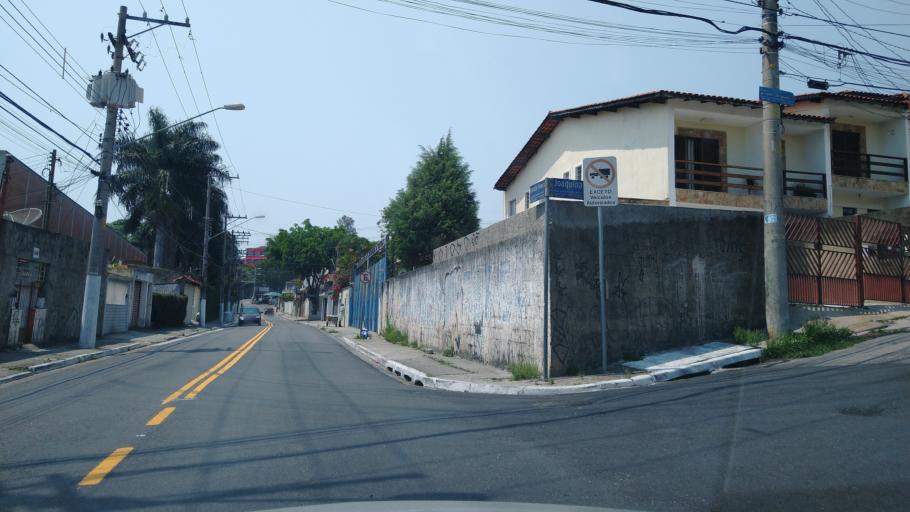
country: BR
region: Sao Paulo
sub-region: Sao Paulo
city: Sao Paulo
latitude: -23.4985
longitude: -46.6021
